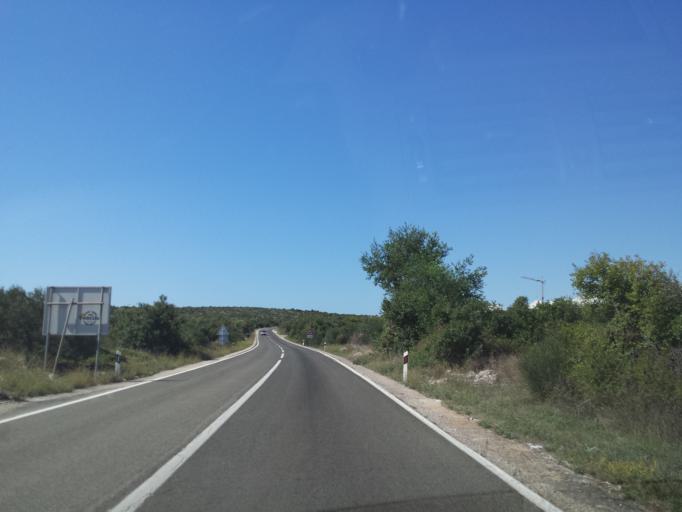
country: HR
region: Sibensko-Kniniska
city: Rogoznica
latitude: 43.5431
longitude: 15.9664
